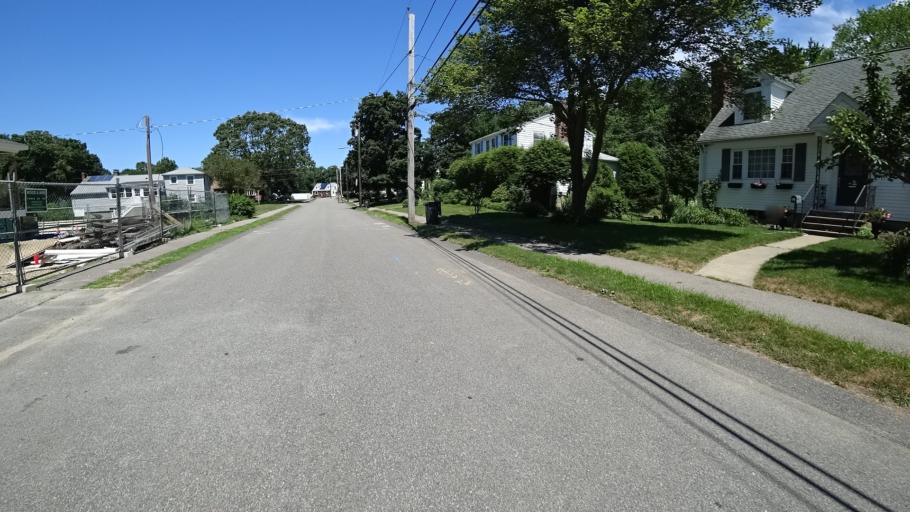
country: US
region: Massachusetts
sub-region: Norfolk County
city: Dedham
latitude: 42.2193
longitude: -71.1510
